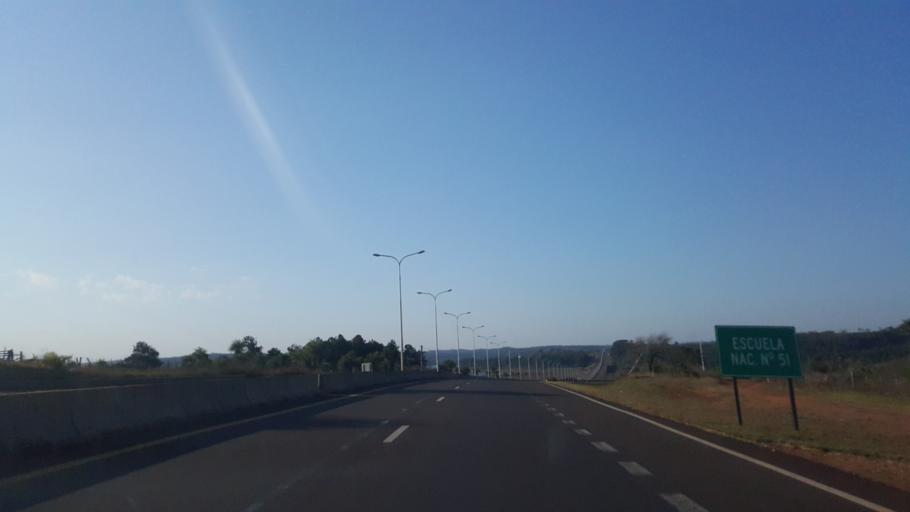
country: AR
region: Misiones
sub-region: Departamento de Candelaria
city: Loreto
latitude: -27.3161
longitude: -55.5451
